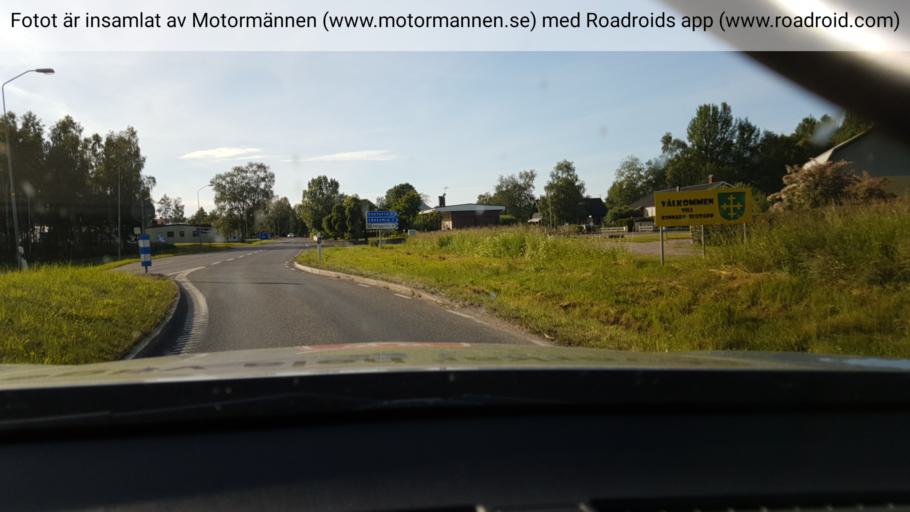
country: SE
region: Vaestra Goetaland
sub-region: Falkopings Kommun
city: Falkoeping
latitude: 58.0696
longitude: 13.5254
